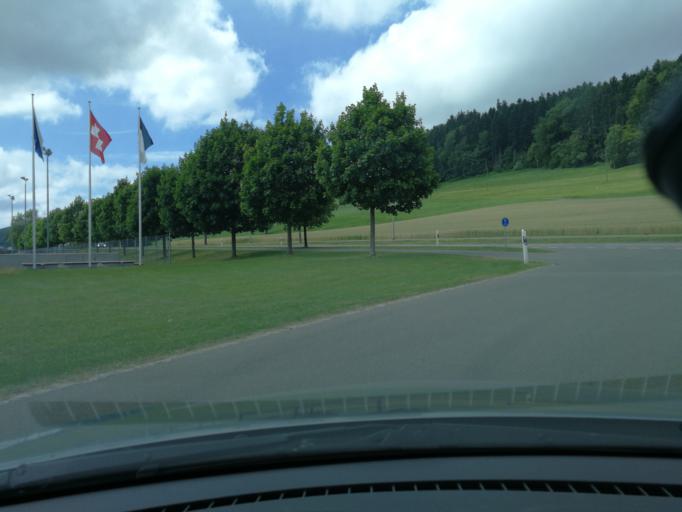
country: CH
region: Zurich
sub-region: Bezirk Uster
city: Aesch
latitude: 47.3382
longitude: 8.6520
